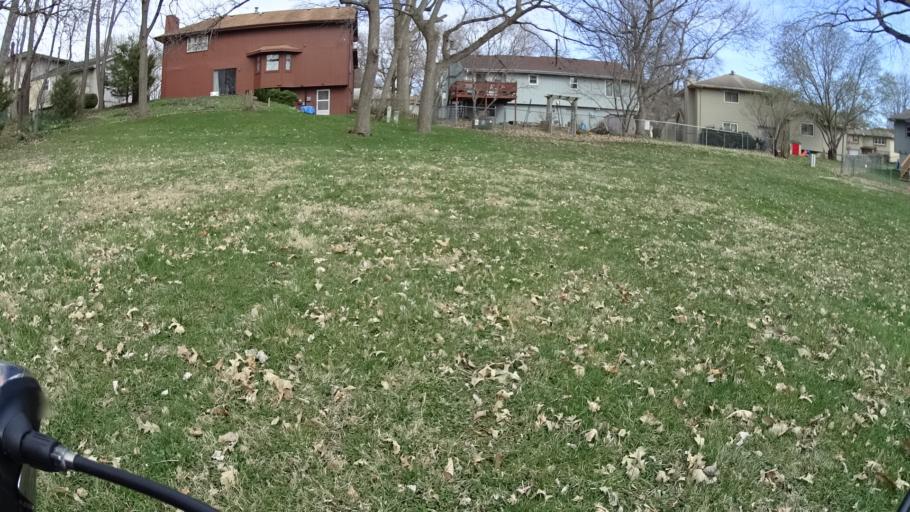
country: US
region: Nebraska
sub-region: Sarpy County
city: Offutt Air Force Base
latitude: 41.1156
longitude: -95.9651
